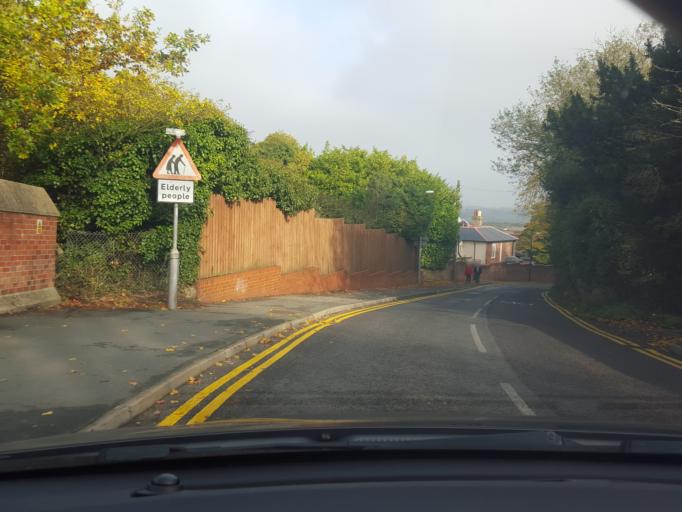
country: GB
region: England
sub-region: Essex
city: Manningtree
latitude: 51.9438
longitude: 1.0594
